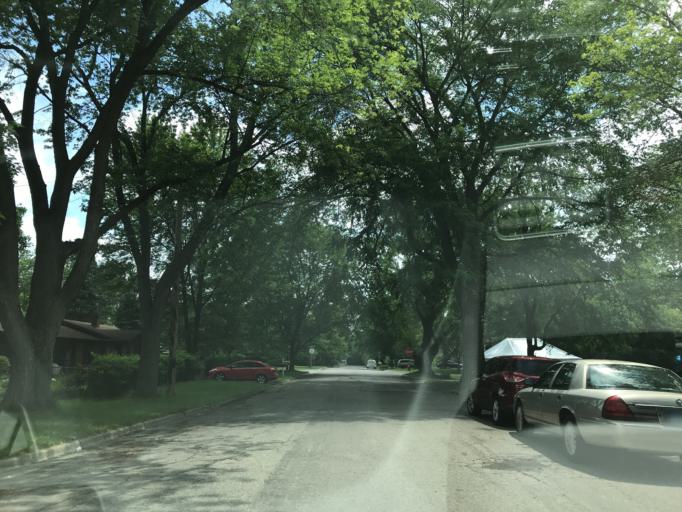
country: US
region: Michigan
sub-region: Washtenaw County
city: Ann Arbor
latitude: 42.2399
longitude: -83.7035
